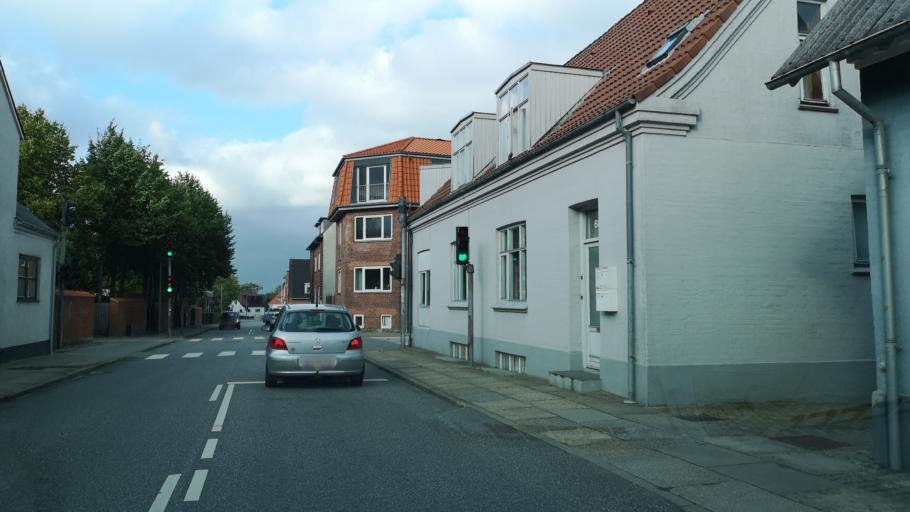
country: DK
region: Central Jutland
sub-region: Herning Kommune
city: Herning
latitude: 56.1403
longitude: 8.9746
